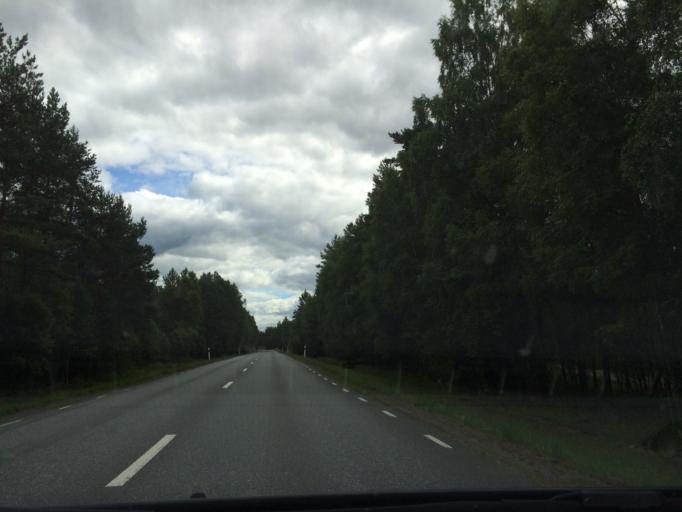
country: SE
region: Joenkoeping
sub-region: Gnosjo Kommun
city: Hillerstorp
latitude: 57.2994
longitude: 13.9290
